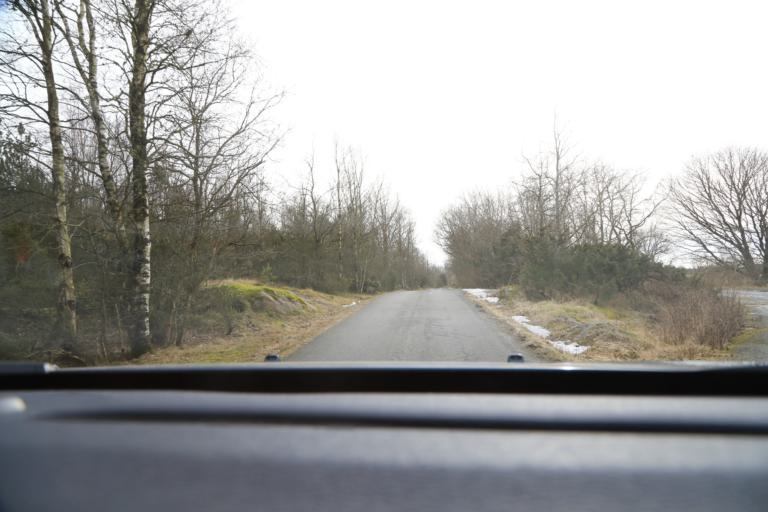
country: SE
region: Halland
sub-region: Varbergs Kommun
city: Veddige
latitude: 57.2164
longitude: 12.2299
